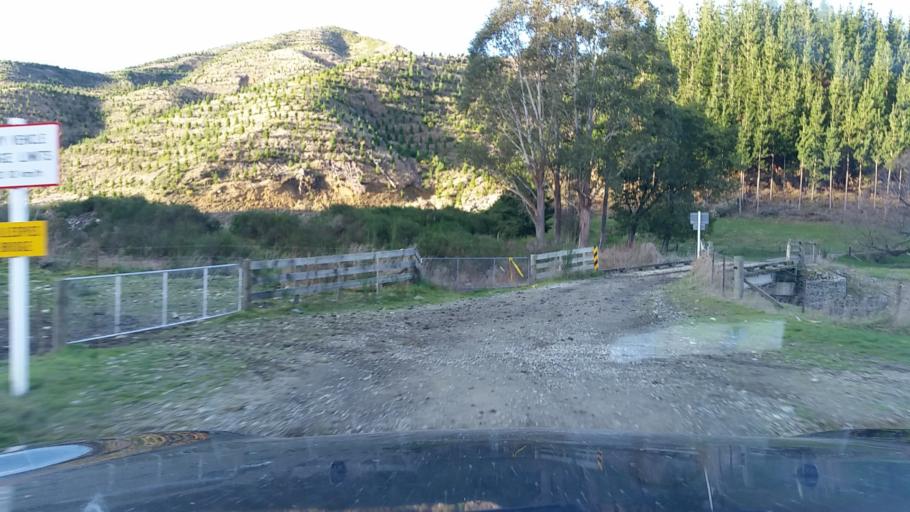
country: NZ
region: Nelson
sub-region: Nelson City
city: Nelson
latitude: -41.5333
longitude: 173.4887
